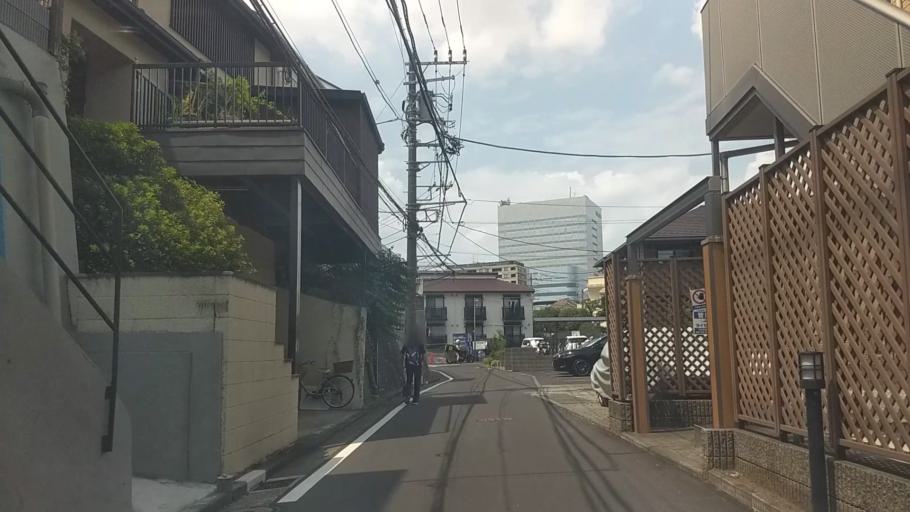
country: JP
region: Kanagawa
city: Yokohama
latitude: 35.5094
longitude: 139.6243
